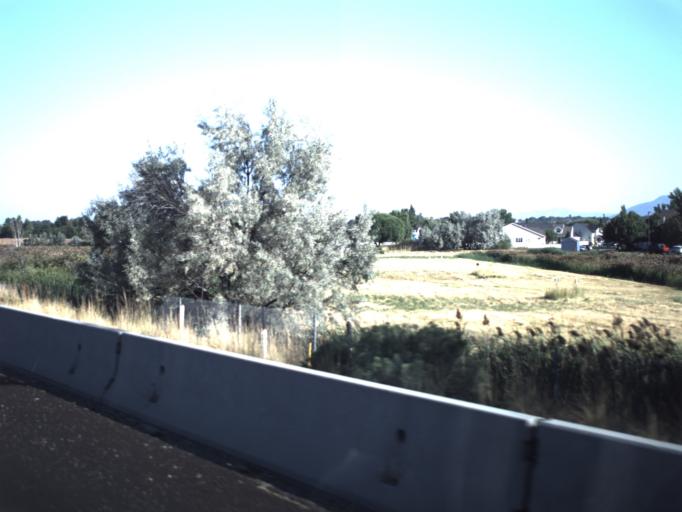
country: US
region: Utah
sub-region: Davis County
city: Farmington
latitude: 40.9923
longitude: -111.9104
